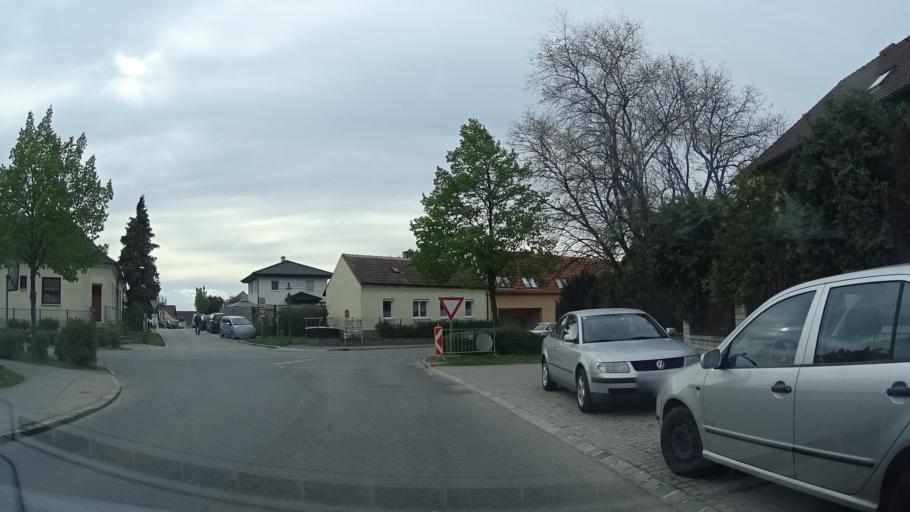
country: AT
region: Lower Austria
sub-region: Politischer Bezirk Korneuburg
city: Stetten
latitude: 48.3656
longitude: 16.3842
